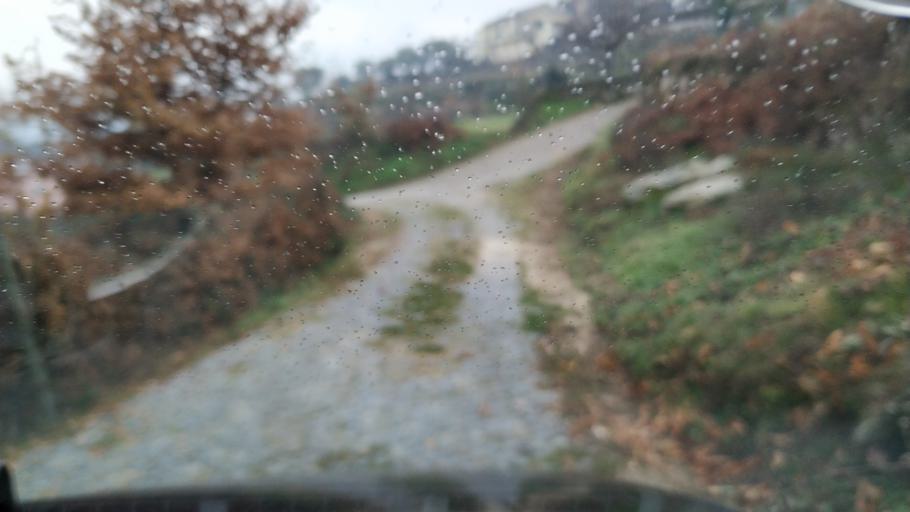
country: PT
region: Vila Real
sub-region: Vila Real
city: Vila Real
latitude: 41.3063
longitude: -7.7808
